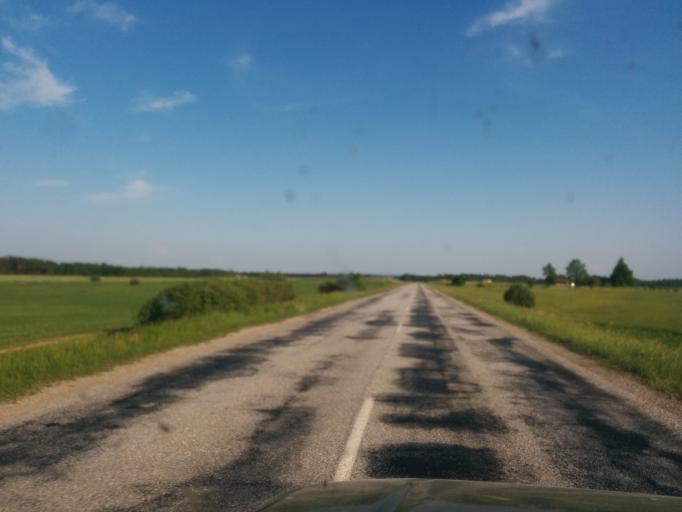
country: LV
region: Talsu Rajons
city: Valdemarpils
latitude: 57.3226
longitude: 22.5263
